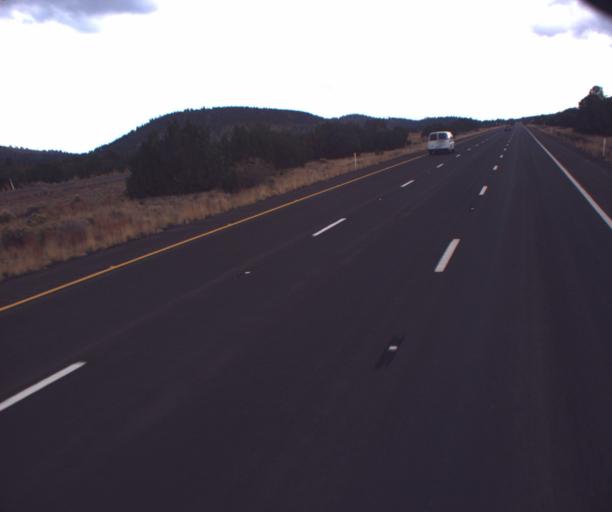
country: US
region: Arizona
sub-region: Coconino County
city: Flagstaff
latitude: 35.4097
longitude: -111.5739
